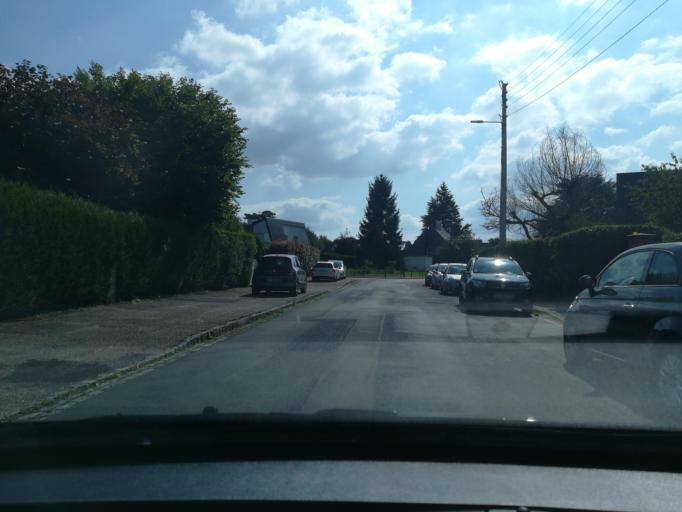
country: FR
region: Haute-Normandie
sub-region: Departement de la Seine-Maritime
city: Bois-Guillaume
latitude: 49.4660
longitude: 1.1116
